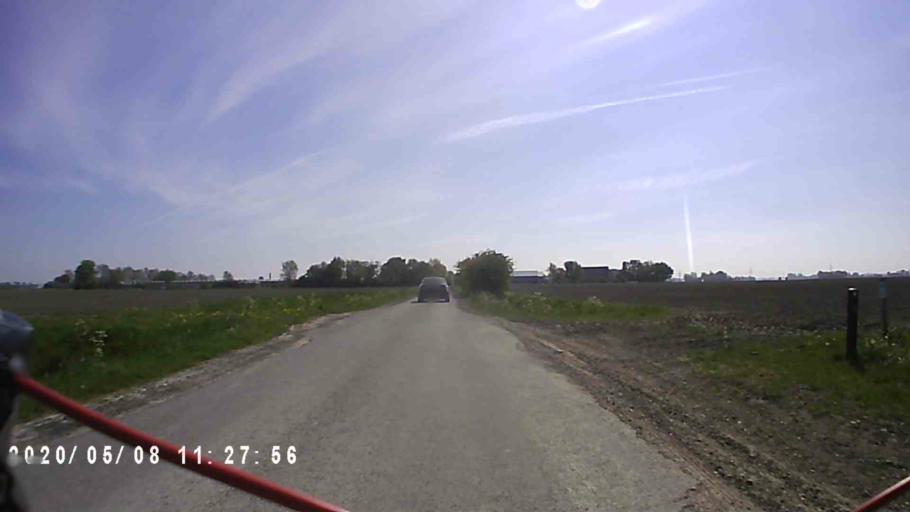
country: NL
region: Groningen
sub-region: Gemeente Bedum
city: Bedum
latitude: 53.3477
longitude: 6.6910
